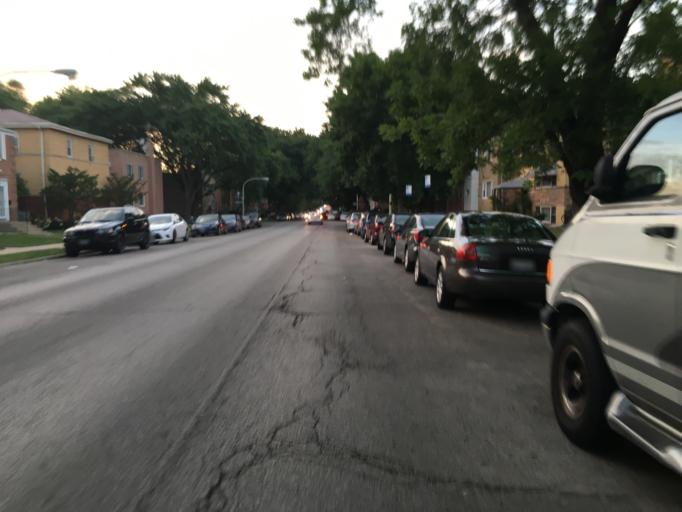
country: US
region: Illinois
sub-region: Cook County
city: Lincolnwood
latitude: 41.9778
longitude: -87.6990
